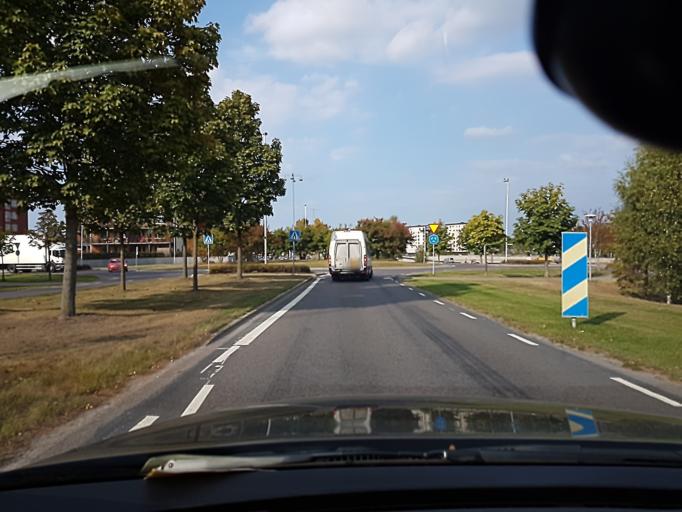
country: SE
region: Kronoberg
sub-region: Vaxjo Kommun
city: Vaexjoe
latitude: 56.8575
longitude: 14.8215
